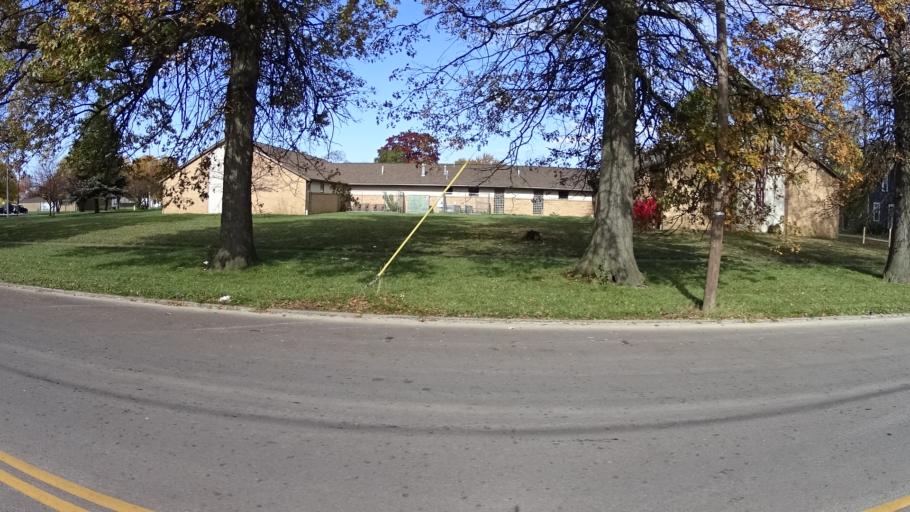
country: US
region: Ohio
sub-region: Lorain County
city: Lorain
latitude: 41.4420
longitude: -82.1453
